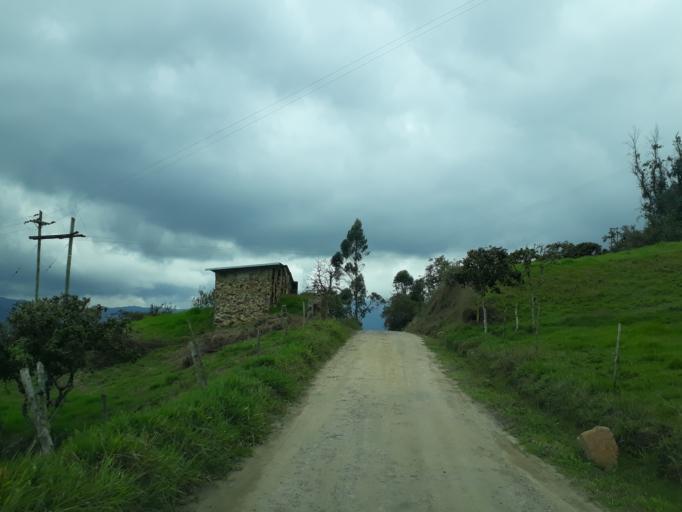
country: CO
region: Cundinamarca
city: Manta
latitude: 5.0175
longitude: -73.5461
